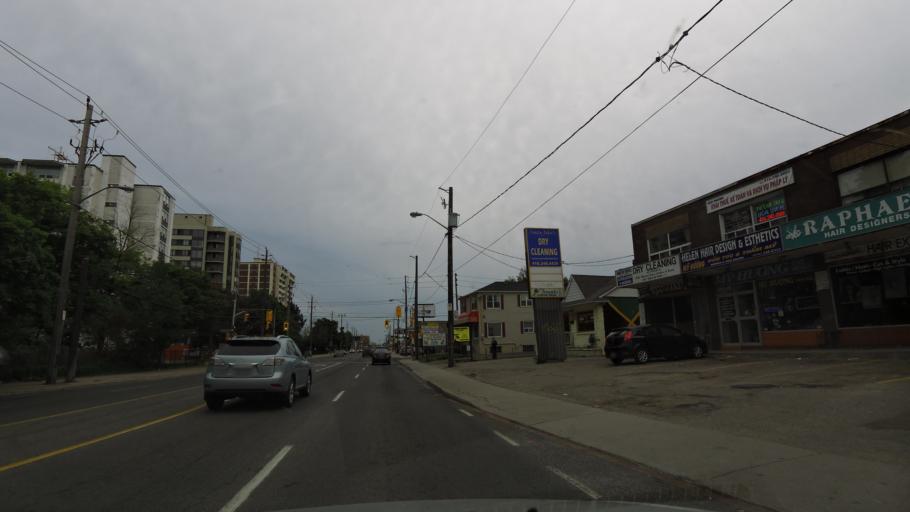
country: CA
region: Ontario
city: Etobicoke
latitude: 43.7073
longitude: -79.5051
